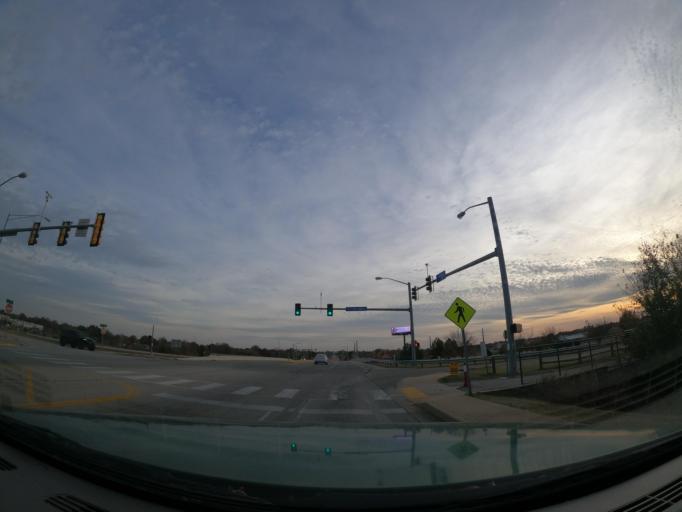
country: US
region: Oklahoma
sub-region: Tulsa County
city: Broken Arrow
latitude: 35.9948
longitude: -95.7975
